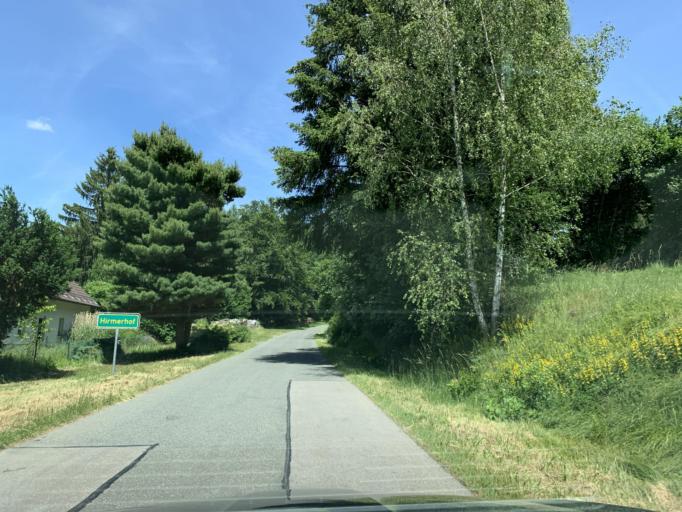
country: DE
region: Bavaria
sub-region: Upper Palatinate
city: Dieterskirchen
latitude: 49.4171
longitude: 12.4371
